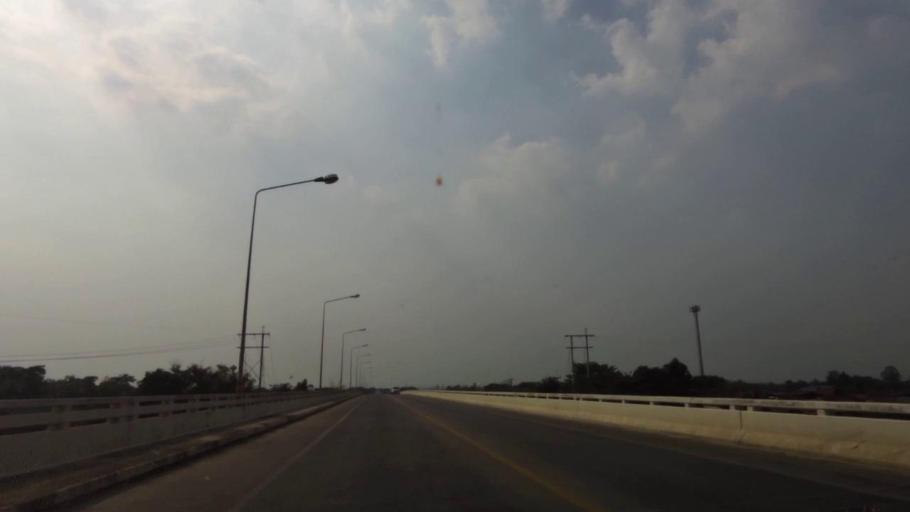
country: TH
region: Phra Nakhon Si Ayutthaya
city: Phra Nakhon Si Ayutthaya
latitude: 14.3038
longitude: 100.5663
